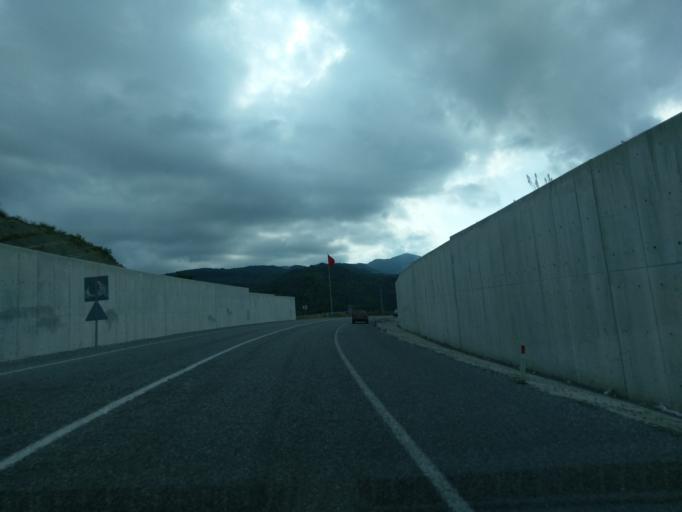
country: TR
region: Sinop
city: Helaldi
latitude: 41.9513
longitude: 34.3859
